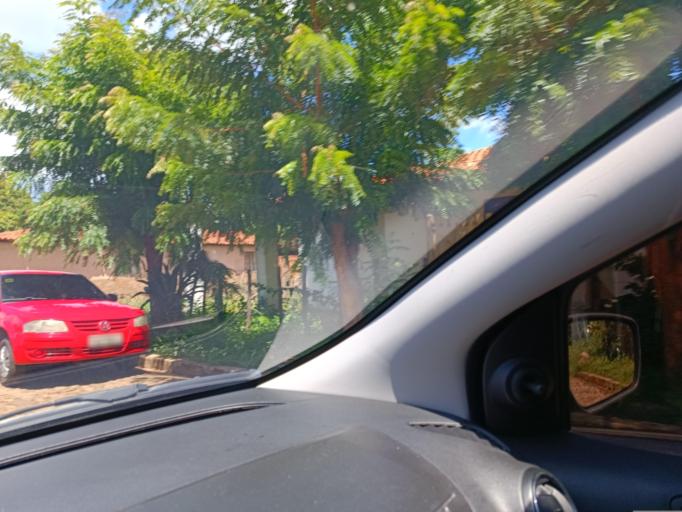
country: BR
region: Piaui
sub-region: Valenca Do Piaui
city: Valenca do Piaui
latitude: -6.1099
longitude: -41.7890
